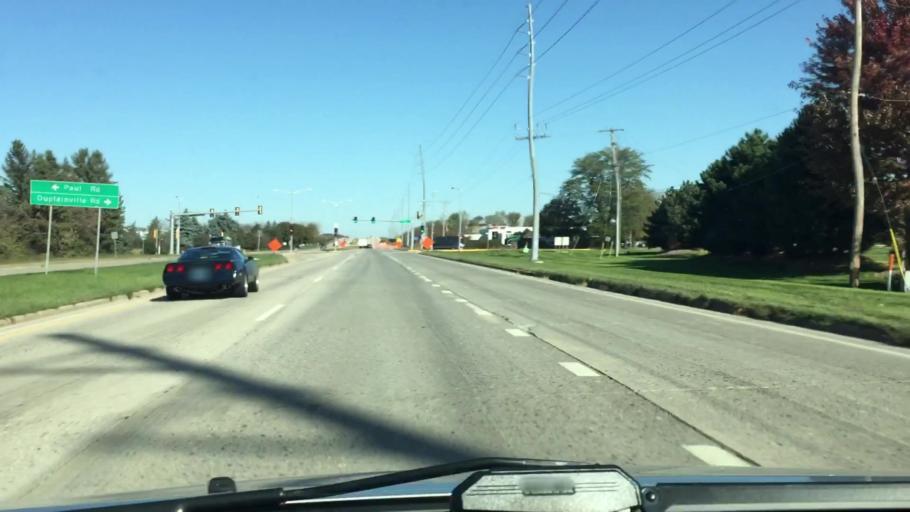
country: US
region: Wisconsin
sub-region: Waukesha County
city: Pewaukee
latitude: 43.0641
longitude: -88.2056
